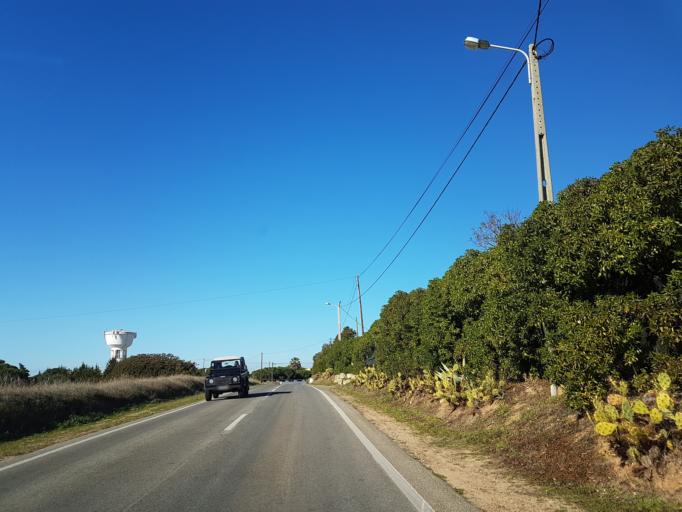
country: PT
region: Faro
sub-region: Lagoa
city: Carvoeiro
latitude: 37.0975
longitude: -8.4404
